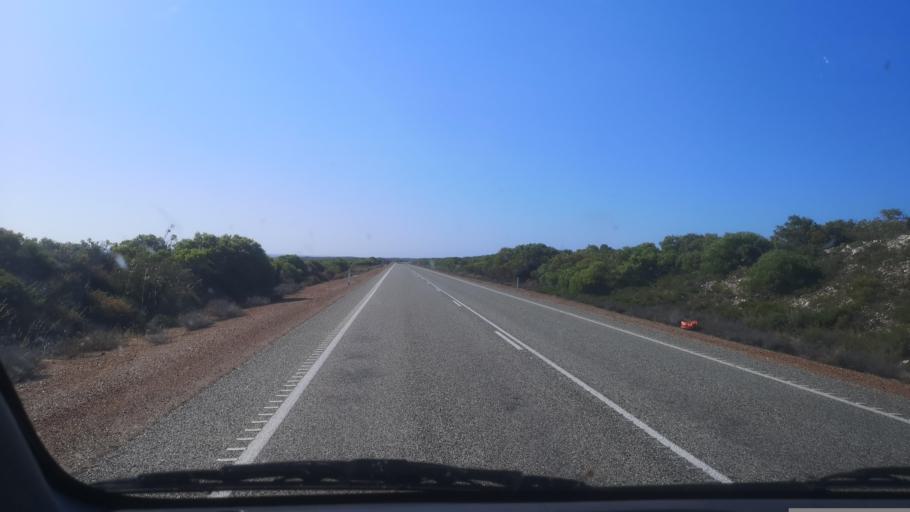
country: AU
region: Western Australia
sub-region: Dandaragan
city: Jurien Bay
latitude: -30.7612
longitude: 115.1983
